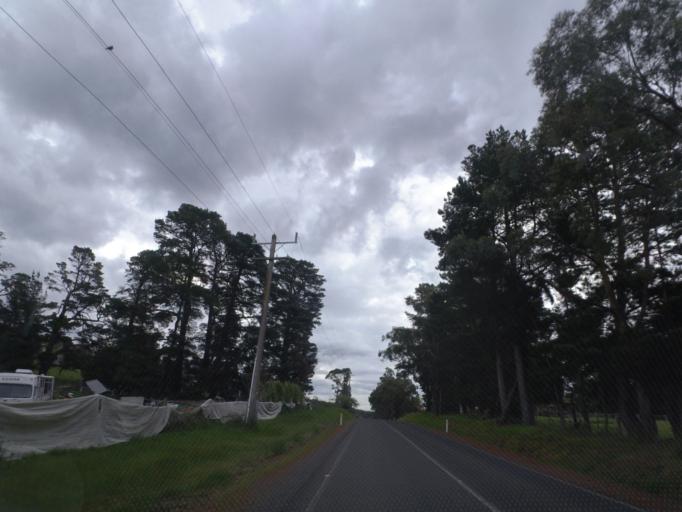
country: AU
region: Victoria
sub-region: Yarra Ranges
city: Mount Evelyn
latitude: -37.7694
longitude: 145.4202
